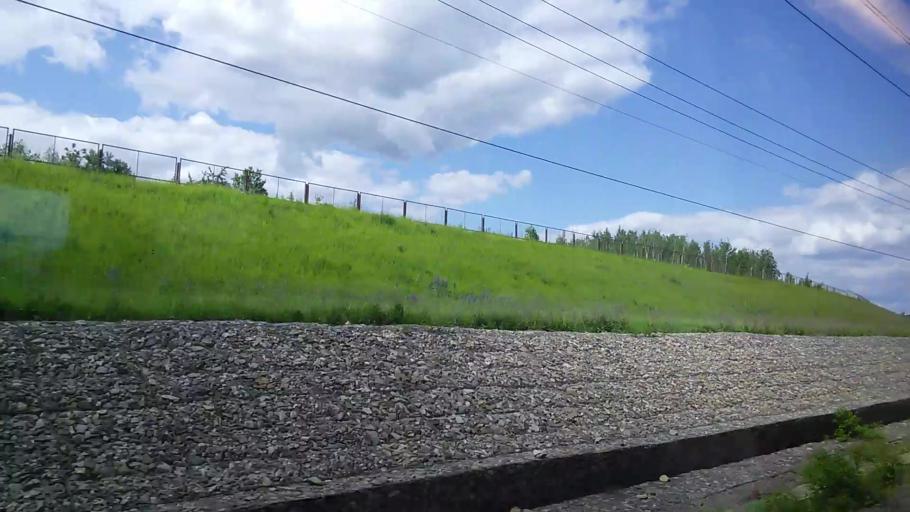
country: RU
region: Moskovskaya
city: Sheremet'yevskiy
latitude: 55.9799
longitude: 37.4669
